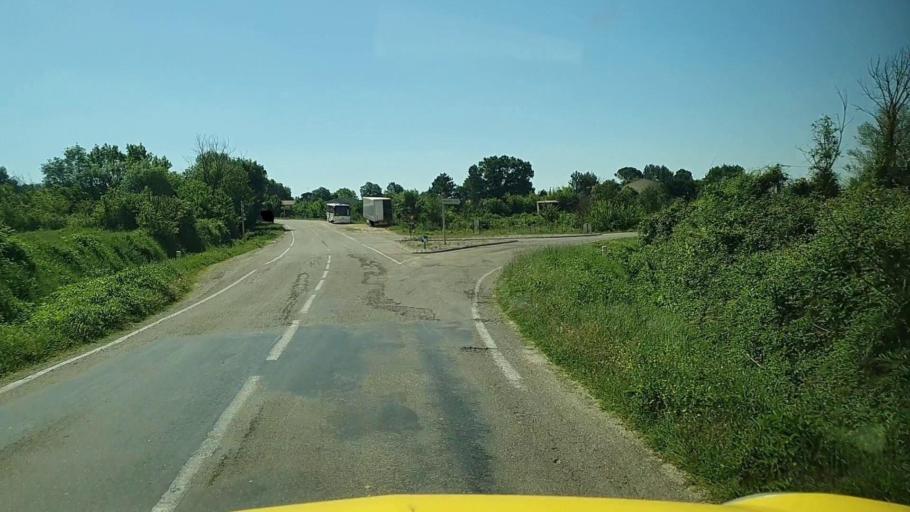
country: FR
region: Languedoc-Roussillon
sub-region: Departement du Gard
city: Moussac
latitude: 43.9889
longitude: 4.2231
